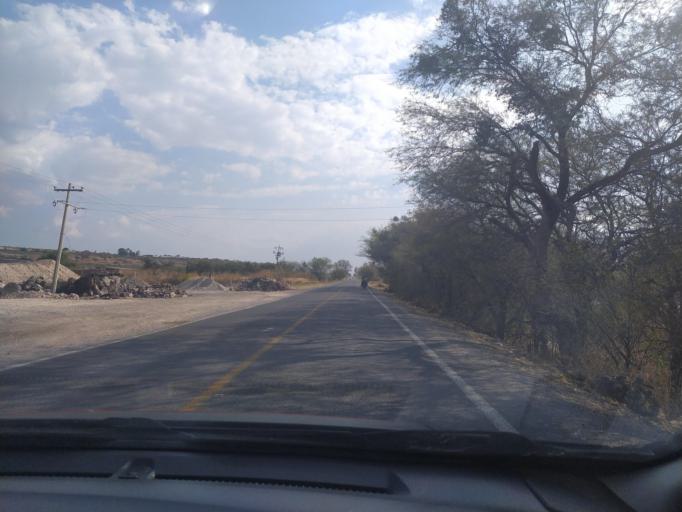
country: MX
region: Guanajuato
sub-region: San Francisco del Rincon
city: San Ignacio de Hidalgo
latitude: 20.8801
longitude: -101.8594
